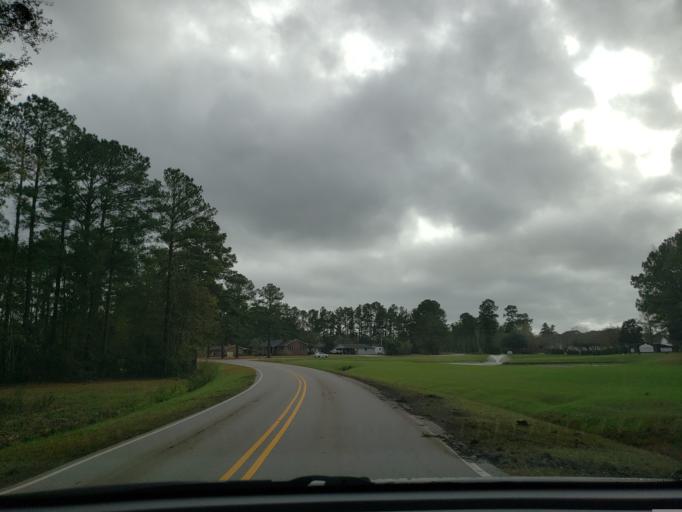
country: US
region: North Carolina
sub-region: Onslow County
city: Jacksonville
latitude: 34.7103
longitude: -77.5806
